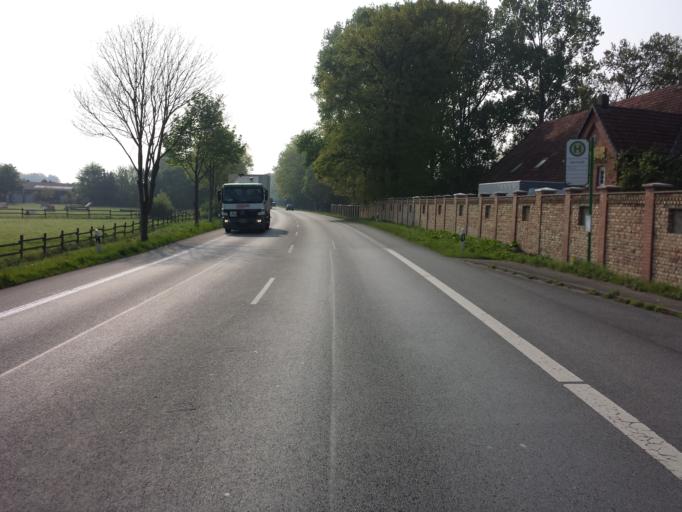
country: DE
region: North Rhine-Westphalia
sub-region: Regierungsbezirk Detmold
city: Guetersloh
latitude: 51.9353
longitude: 8.3043
